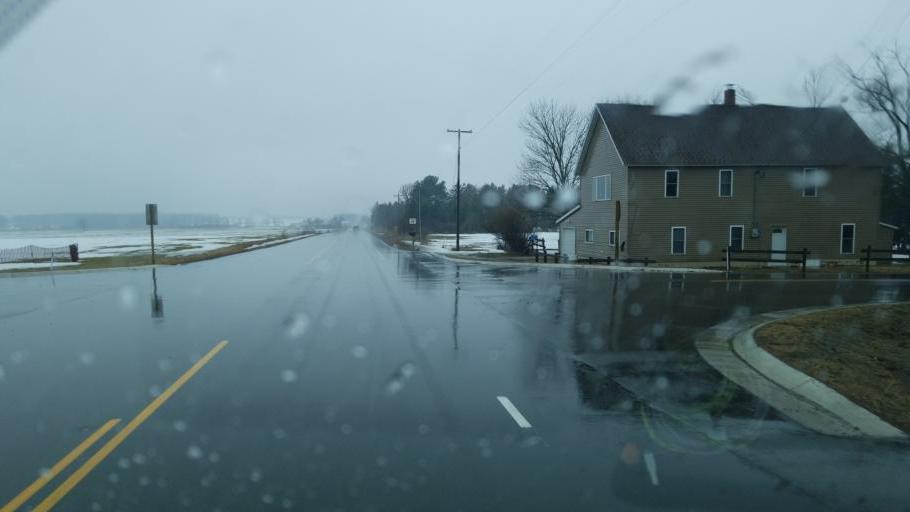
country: US
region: Wisconsin
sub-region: Marathon County
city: Spencer
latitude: 44.6563
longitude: -90.2992
